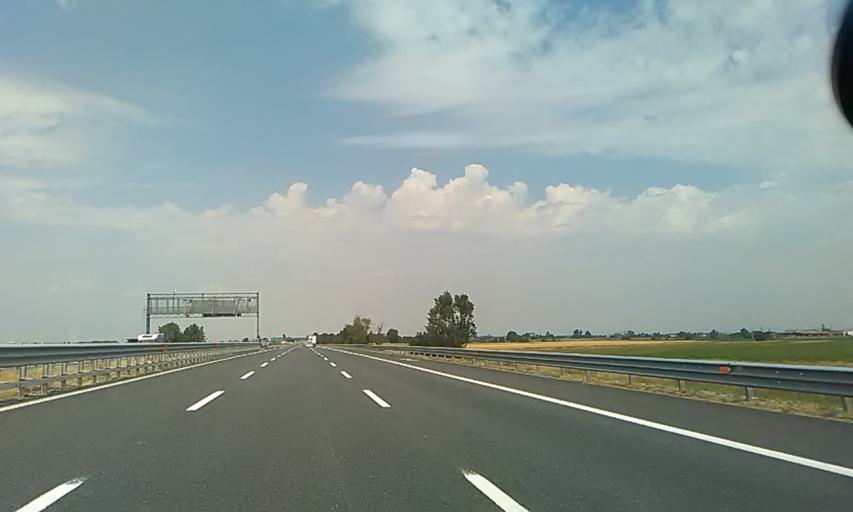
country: IT
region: Piedmont
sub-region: Provincia di Alessandria
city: Predosa
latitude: 44.7708
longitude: 8.6304
